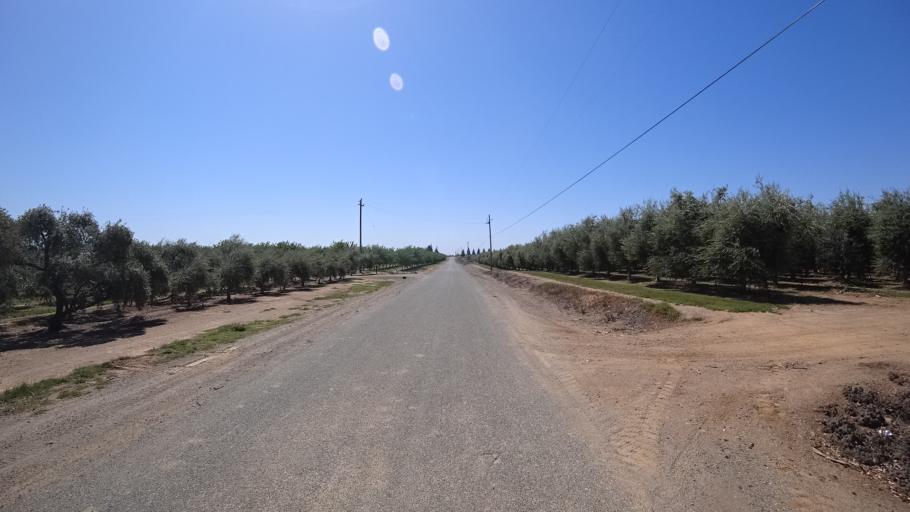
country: US
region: California
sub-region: Glenn County
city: Orland
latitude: 39.7912
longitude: -122.1691
